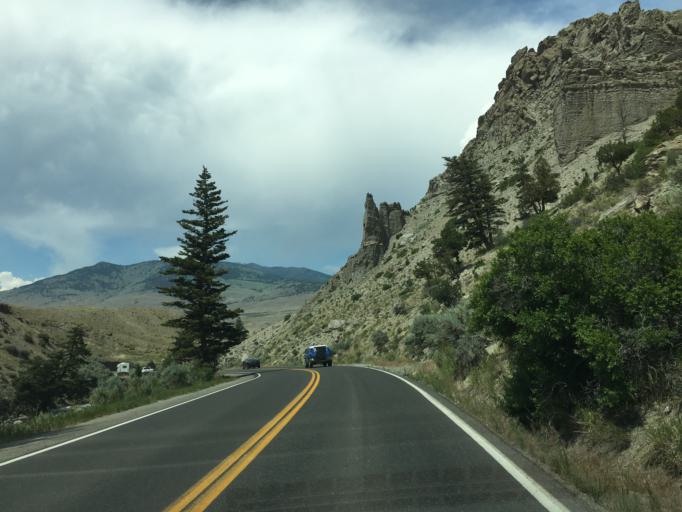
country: US
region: Montana
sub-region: Gallatin County
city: West Yellowstone
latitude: 45.0097
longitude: -110.6938
